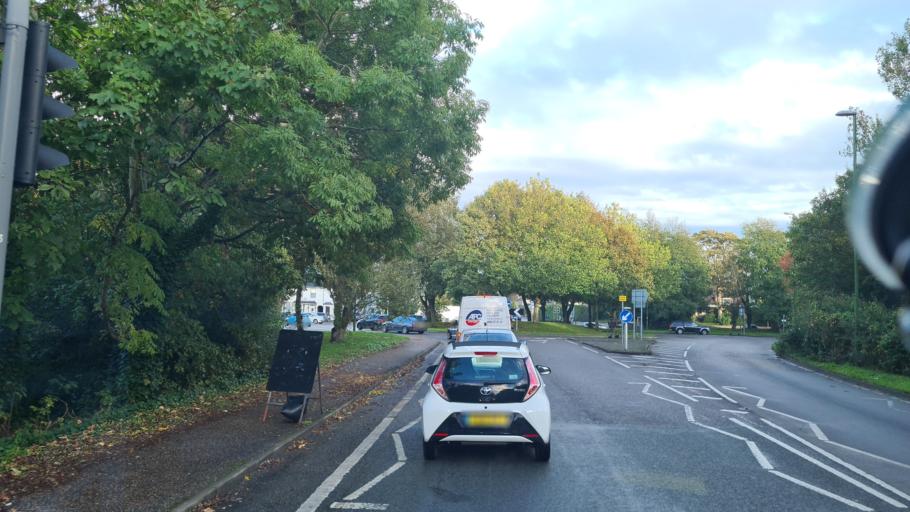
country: GB
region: England
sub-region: West Sussex
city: Littlehampton
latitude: 50.8216
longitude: -0.5452
